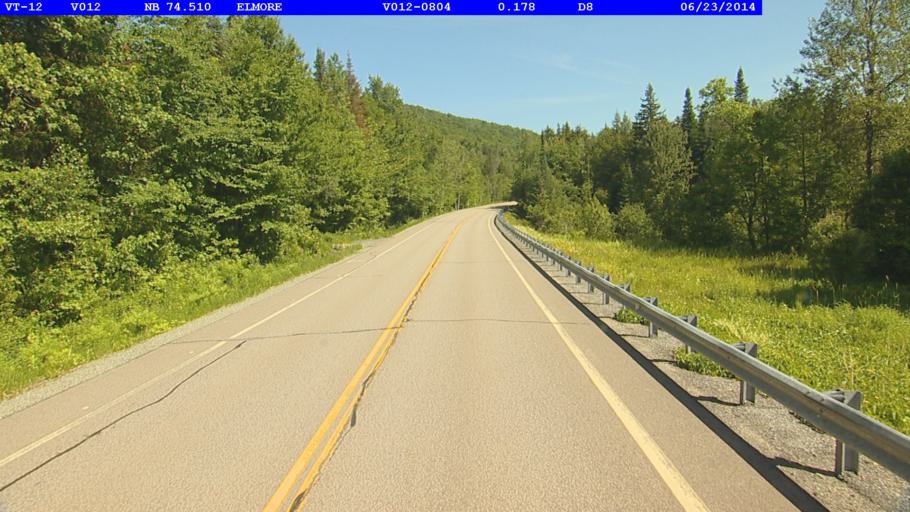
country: US
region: Vermont
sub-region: Lamoille County
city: Morrisville
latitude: 44.4546
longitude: -72.5470
